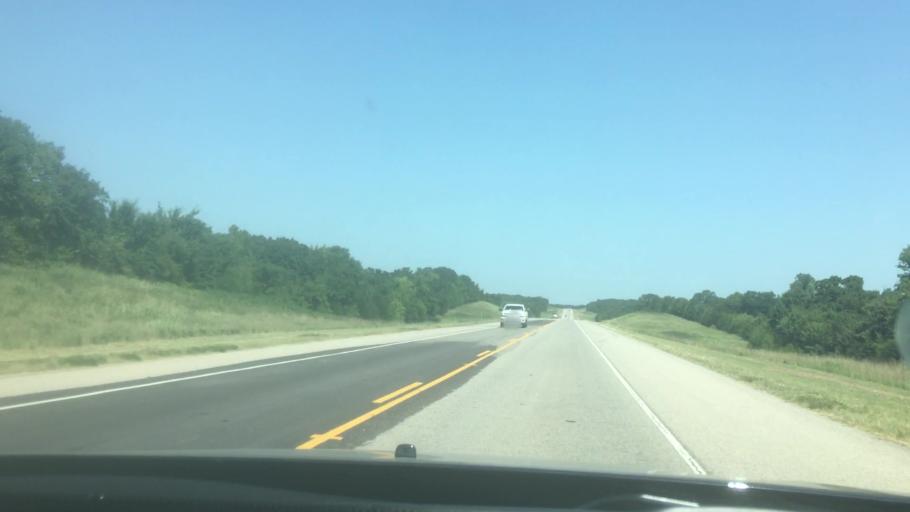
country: US
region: Oklahoma
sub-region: Pontotoc County
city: Ada
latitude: 34.6563
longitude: -96.5580
